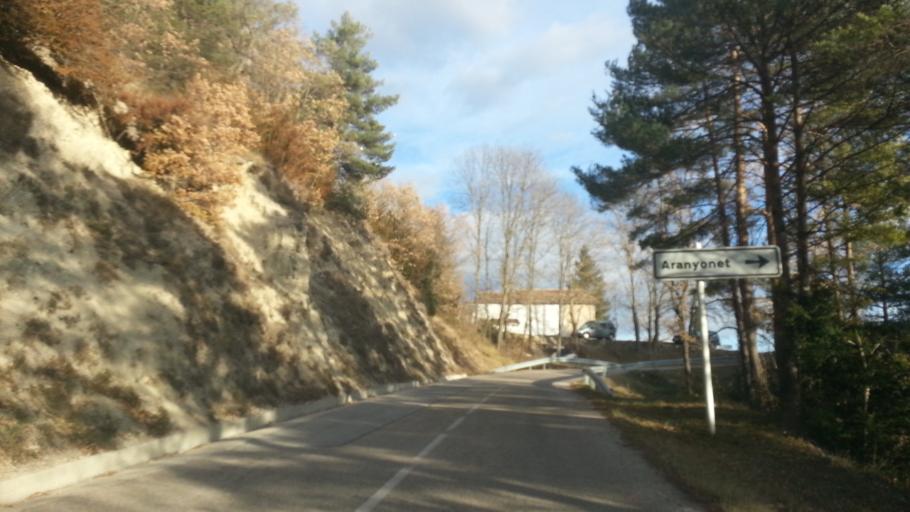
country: ES
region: Catalonia
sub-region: Provincia de Girona
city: Toses
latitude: 42.2470
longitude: 2.0401
